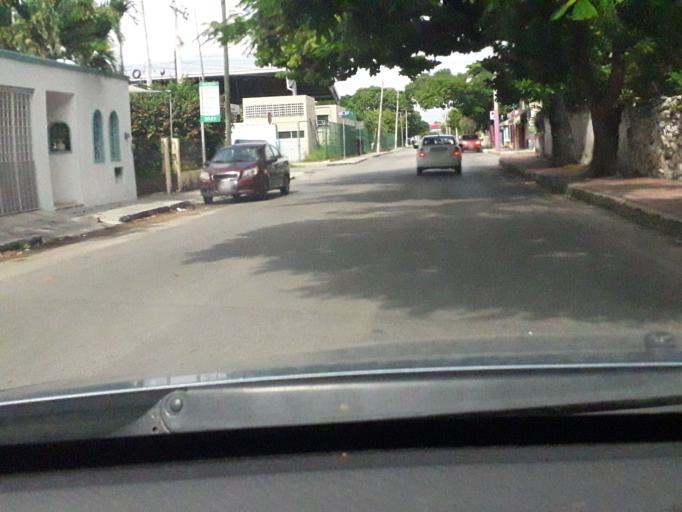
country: MX
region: Yucatan
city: Merida
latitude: 20.9797
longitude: -89.6553
